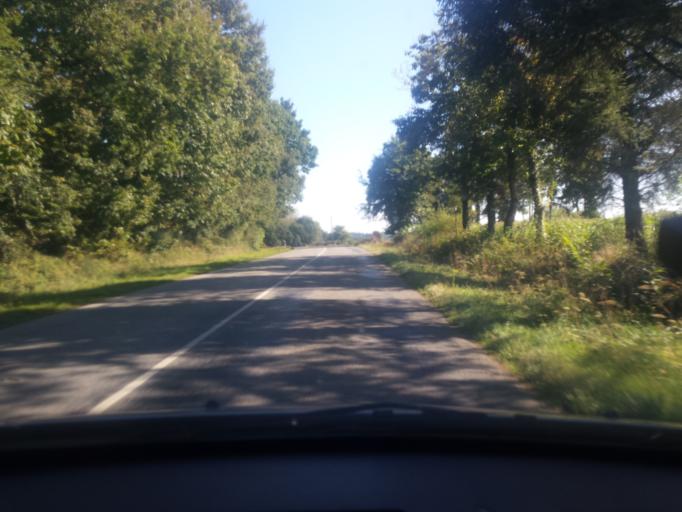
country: FR
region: Brittany
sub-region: Departement du Morbihan
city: Cleguerec
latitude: 48.1034
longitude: -3.1076
